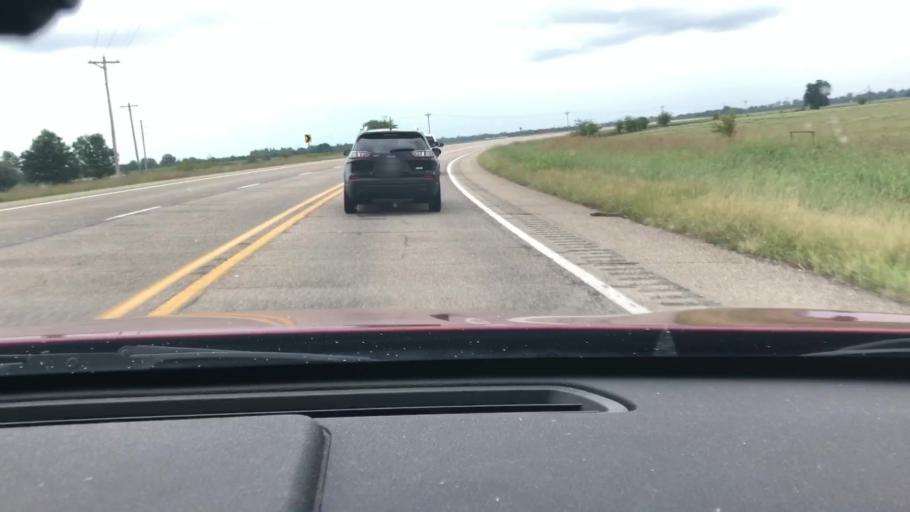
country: US
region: Arkansas
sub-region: Lafayette County
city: Lewisville
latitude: 33.3923
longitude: -93.7375
